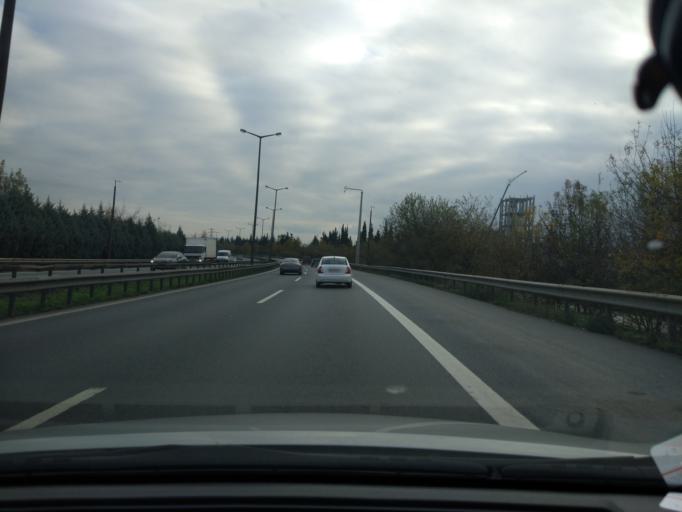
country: TR
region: Kocaeli
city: Kosekoy
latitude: 40.7701
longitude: 29.9890
